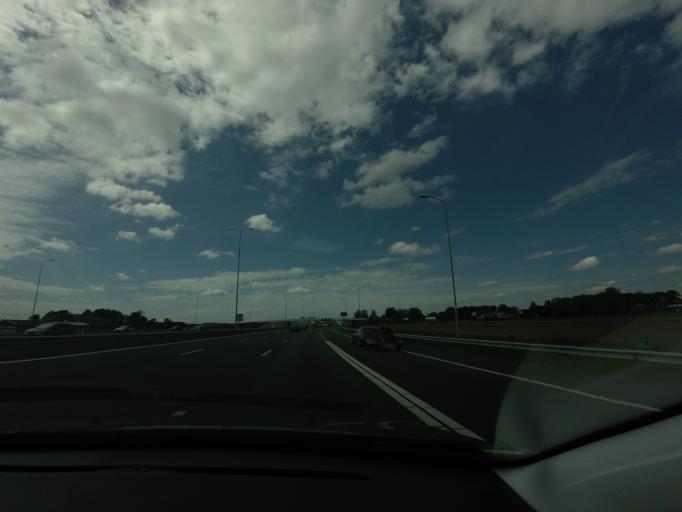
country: NL
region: North Holland
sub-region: Gemeente Aalsmeer
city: Aalsmeer
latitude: 52.3287
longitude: 4.7719
